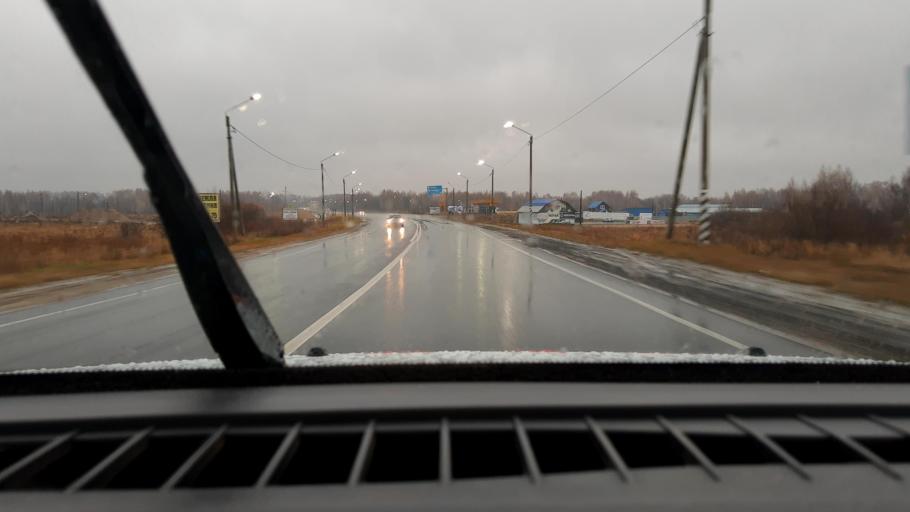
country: RU
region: Nizjnij Novgorod
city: Sitniki
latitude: 56.4984
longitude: 44.0253
